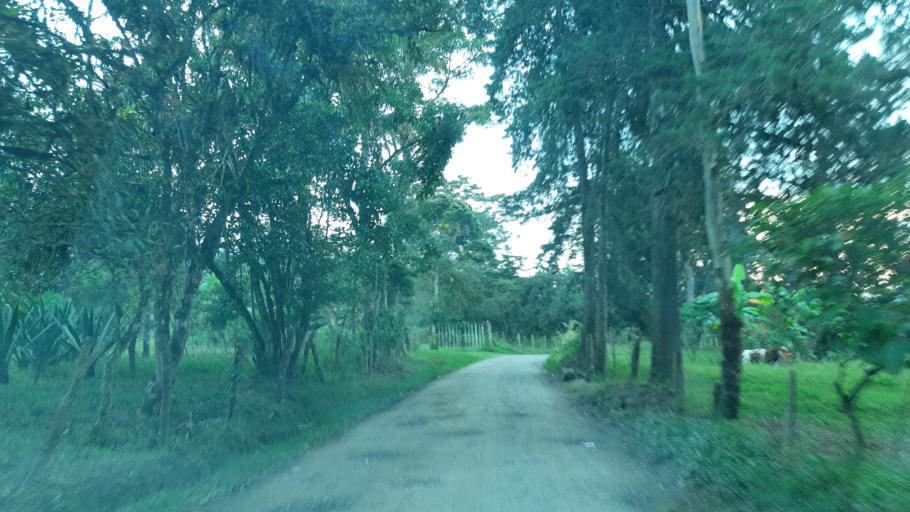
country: CO
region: Boyaca
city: Garagoa
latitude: 5.1048
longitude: -73.3569
